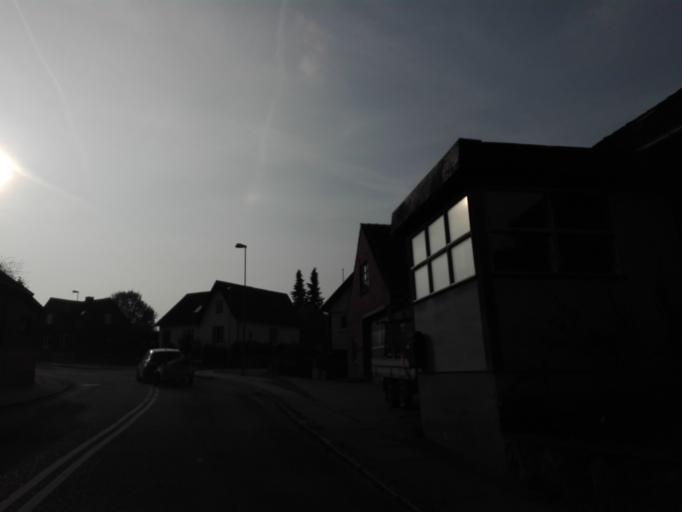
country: DK
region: Central Jutland
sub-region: Arhus Kommune
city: Marslet
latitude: 56.0663
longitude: 10.1609
